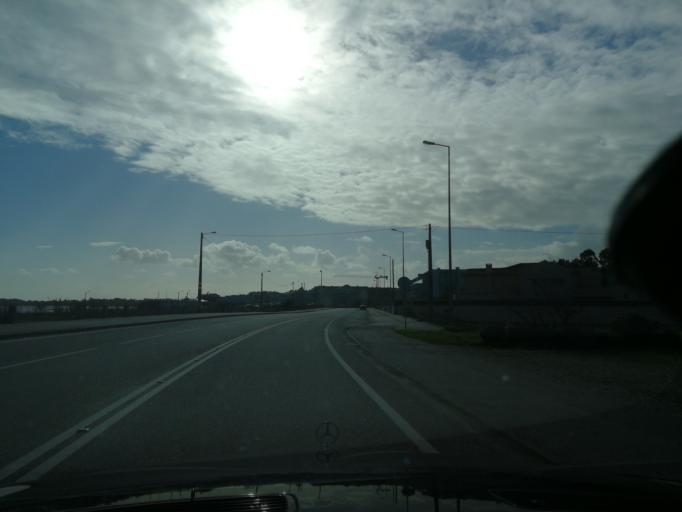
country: PT
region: Aveiro
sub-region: Murtosa
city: Murtosa
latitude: 40.7677
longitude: -8.6961
